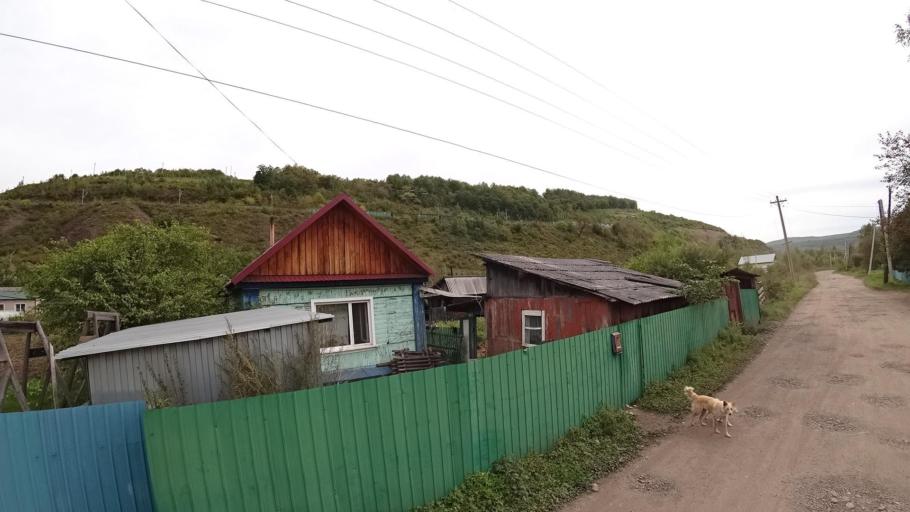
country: RU
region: Jewish Autonomous Oblast
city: Khingansk
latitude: 48.9942
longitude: 131.0551
